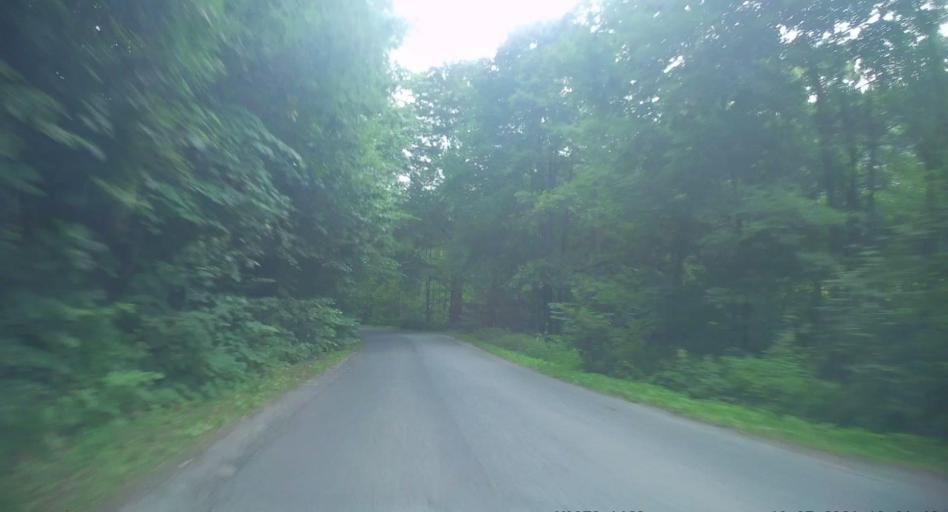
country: PL
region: Lower Silesian Voivodeship
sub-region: Powiat klodzki
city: Ludwikowice Klodzkie
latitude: 50.6349
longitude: 16.4636
